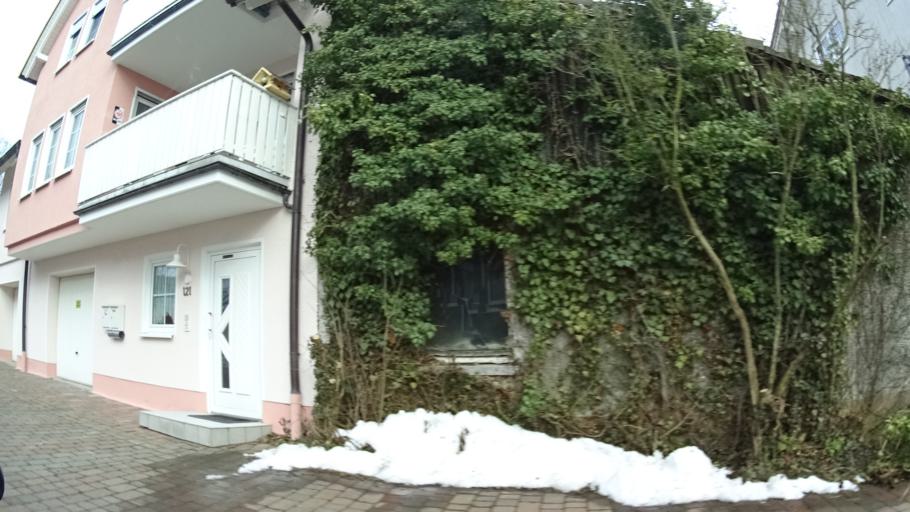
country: DE
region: Hesse
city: Michelstadt
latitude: 49.6567
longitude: 9.0677
